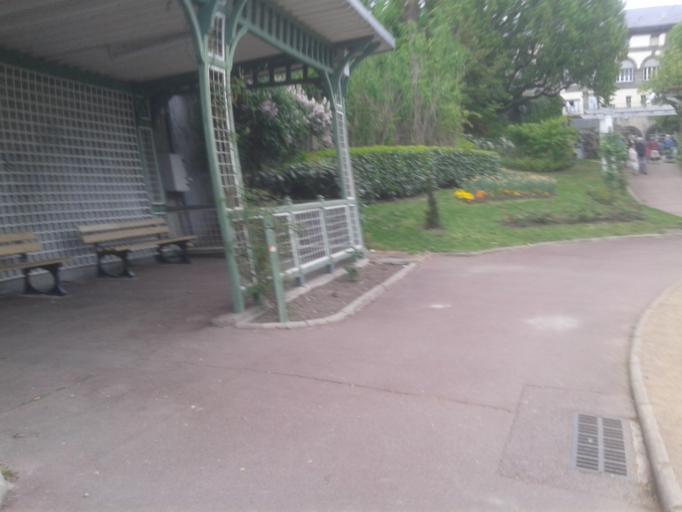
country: FR
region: Auvergne
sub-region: Departement du Puy-de-Dome
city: Clermont-Ferrand
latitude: 45.7717
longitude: 3.0872
